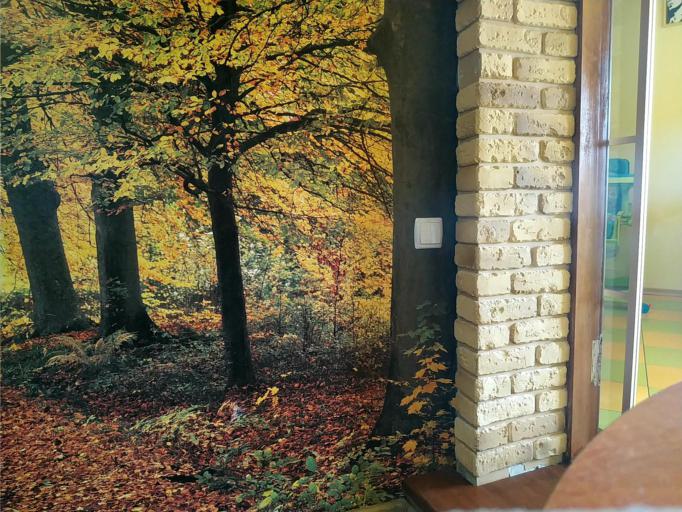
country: RU
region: Smolensk
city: Katyn'
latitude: 54.9446
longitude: 31.7180
